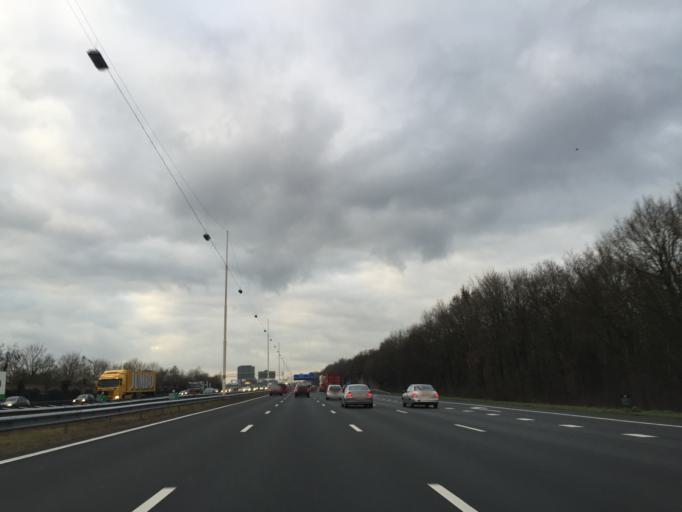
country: NL
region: Utrecht
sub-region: Gemeente IJsselstein
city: IJsselstein
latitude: 52.0704
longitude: 5.0473
